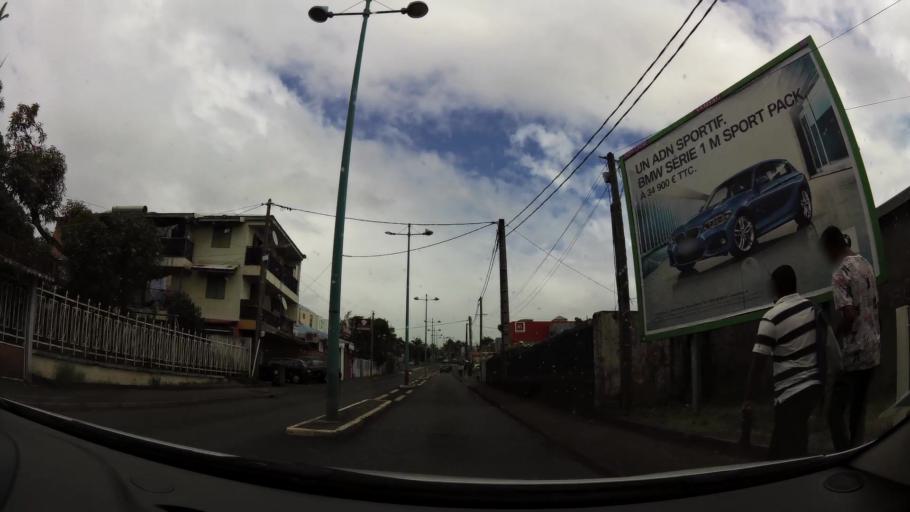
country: RE
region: Reunion
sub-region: Reunion
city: Sainte-Suzanne
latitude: -20.9036
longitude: 55.6010
